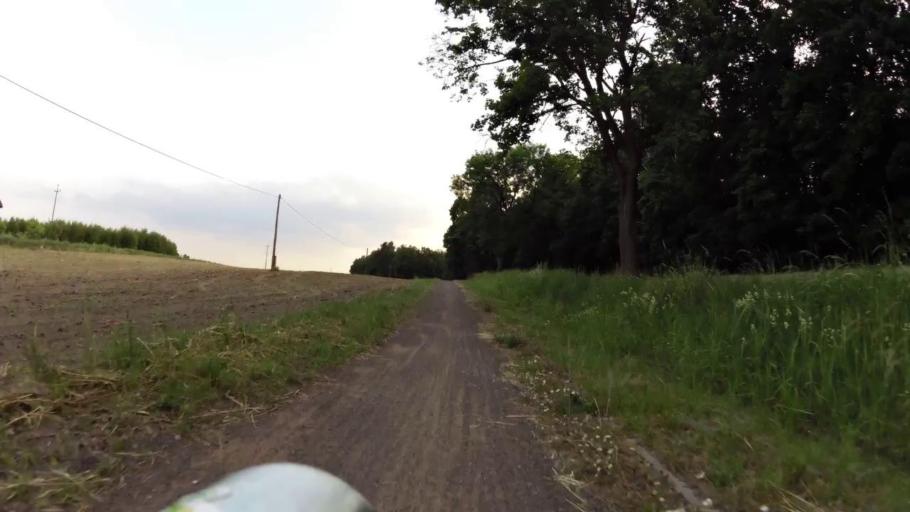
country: PL
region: Kujawsko-Pomorskie
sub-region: Powiat bydgoski
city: Dabrowa Chelminska
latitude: 53.1860
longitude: 18.3395
